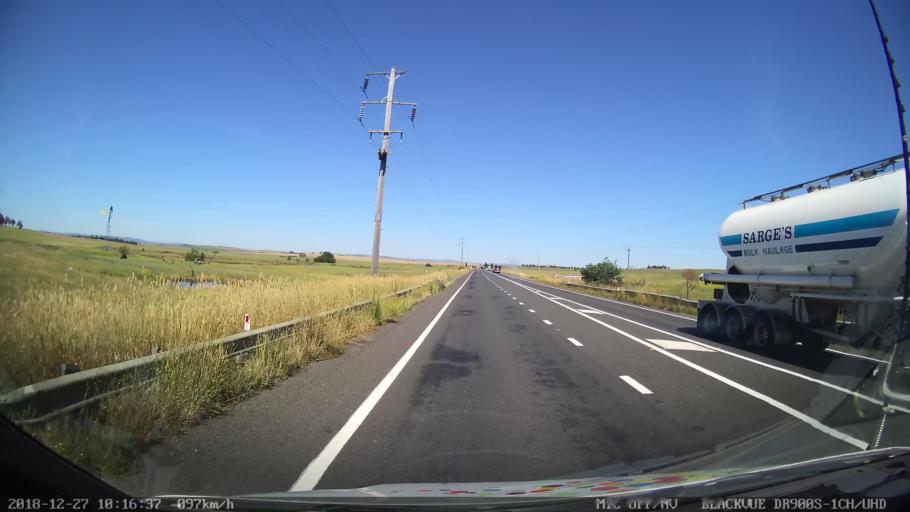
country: AU
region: New South Wales
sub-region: Bathurst Regional
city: Kelso
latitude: -33.4260
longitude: 149.6925
